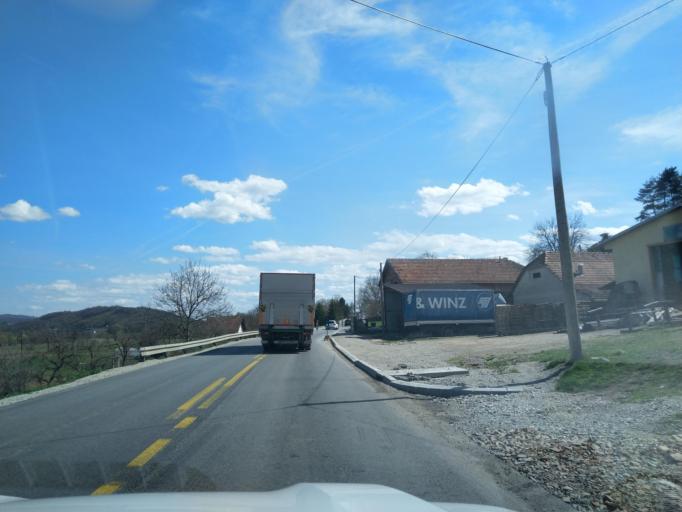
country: RS
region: Central Serbia
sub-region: Zlatiborski Okrug
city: Pozega
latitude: 43.8257
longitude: 20.0798
